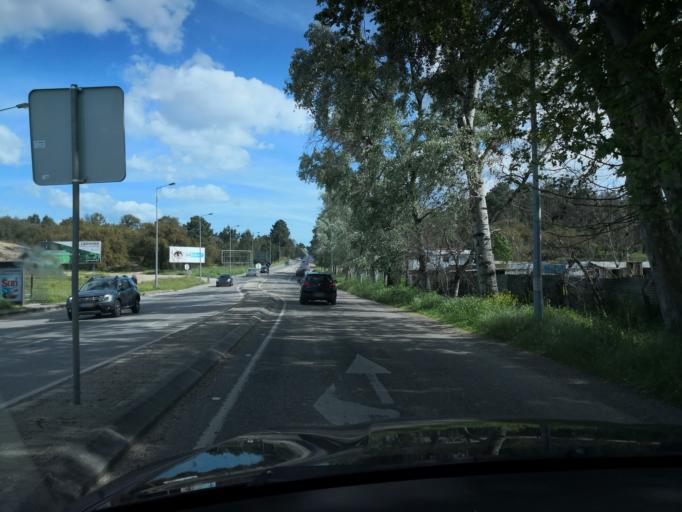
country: PT
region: Setubal
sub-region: Barreiro
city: Santo Antonio da Charneca
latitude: 38.5541
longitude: -9.0346
